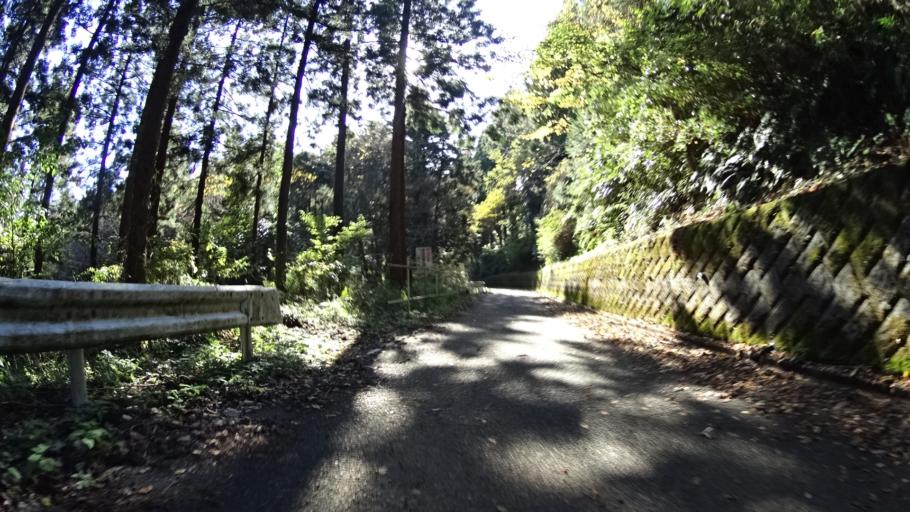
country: JP
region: Kanagawa
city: Zama
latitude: 35.5212
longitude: 139.2750
